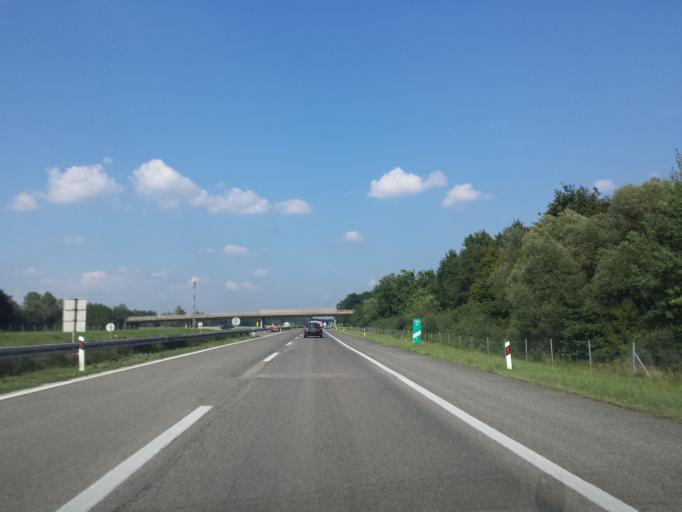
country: HR
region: Zagrebacka
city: Jastrebarsko
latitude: 45.6442
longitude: 15.6779
